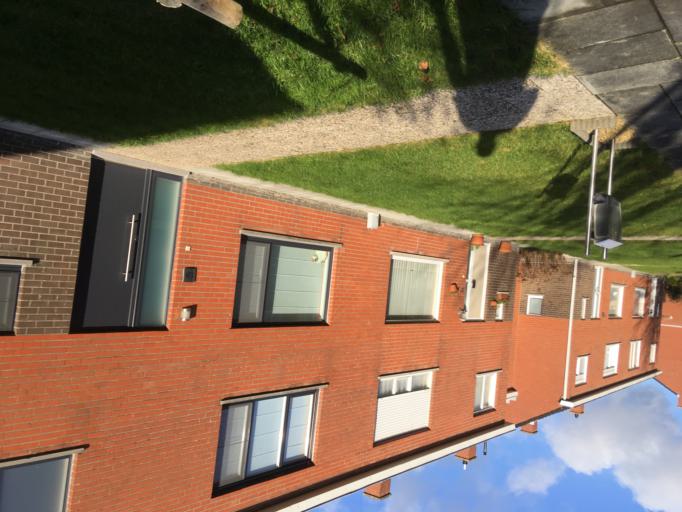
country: BE
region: Flanders
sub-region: Provincie West-Vlaanderen
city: Roeselare
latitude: 50.9631
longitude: 3.1111
